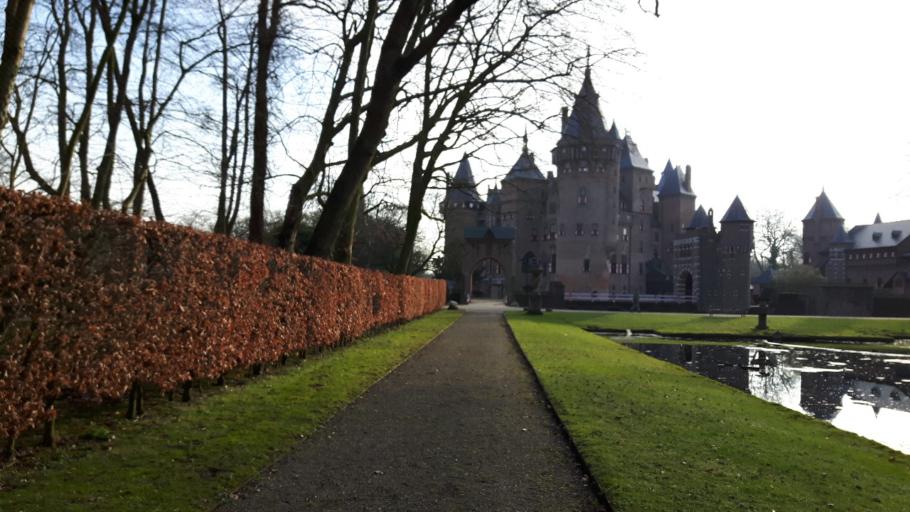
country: NL
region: Utrecht
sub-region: Stichtse Vecht
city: Spechtenkamp
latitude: 52.1227
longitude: 4.9864
